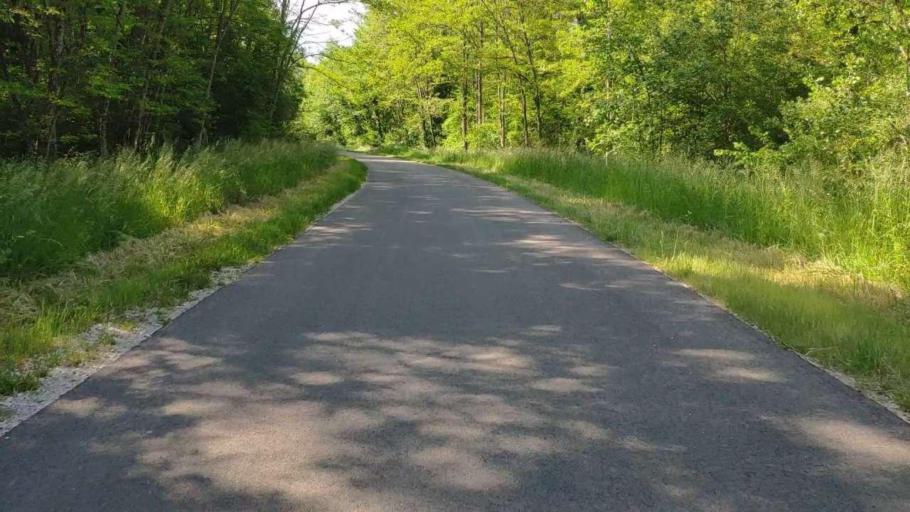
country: FR
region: Franche-Comte
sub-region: Departement du Jura
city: Bletterans
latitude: 46.7006
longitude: 5.4710
